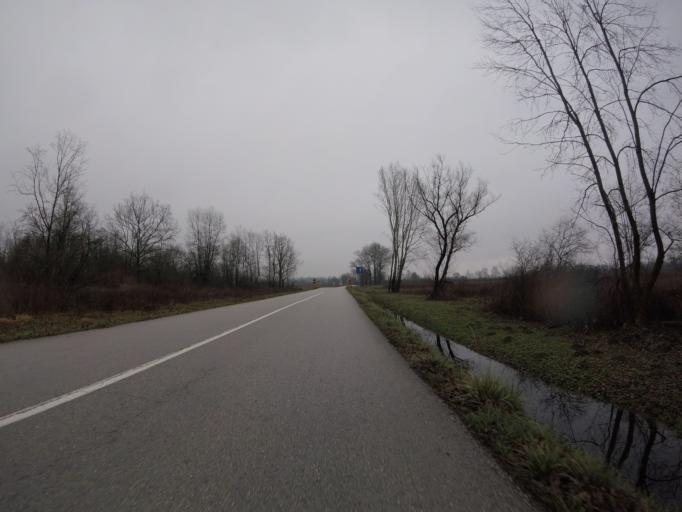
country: HR
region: Zagrebacka
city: Kuce
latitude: 45.7040
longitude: 16.1984
